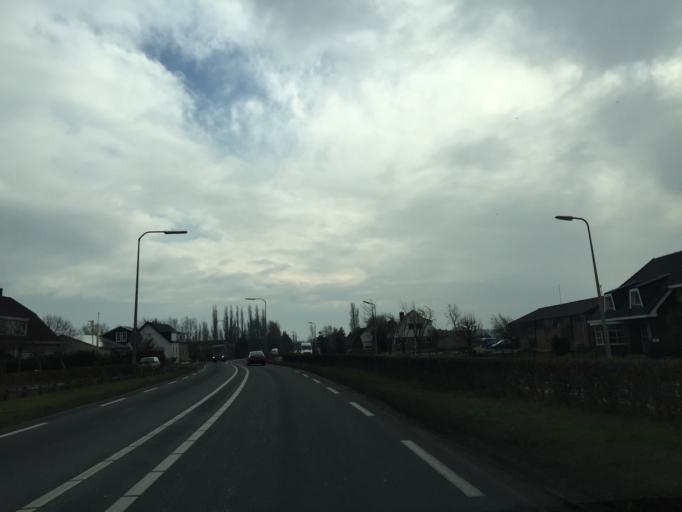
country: NL
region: South Holland
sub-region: Gemeente Capelle aan den IJssel
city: Capelle aan den IJssel
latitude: 51.9882
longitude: 4.6015
